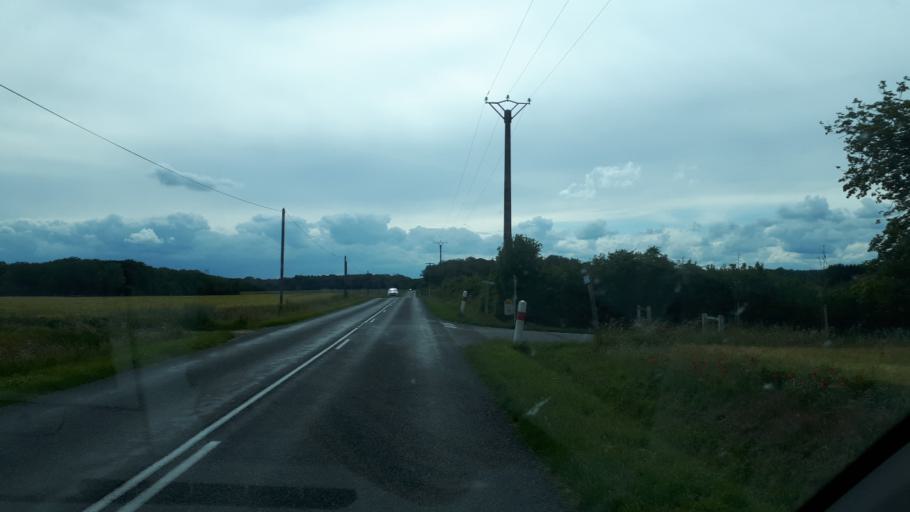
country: FR
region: Centre
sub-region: Departement du Cher
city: La Chapelle-Saint-Ursin
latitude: 47.0797
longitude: 2.3076
